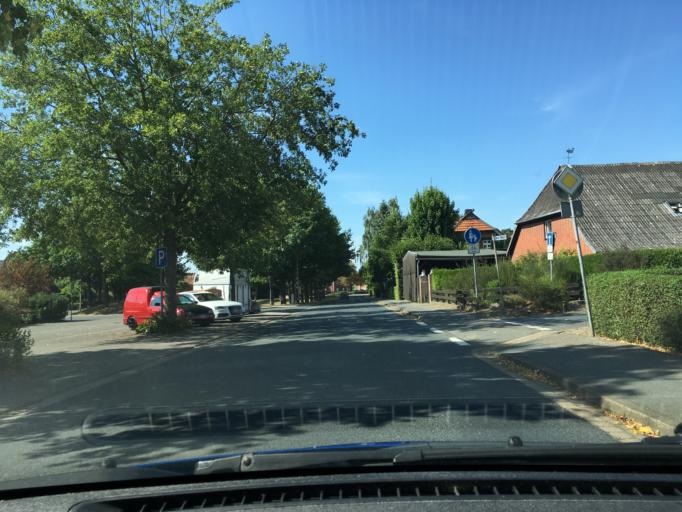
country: DE
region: Lower Saxony
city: Bardowick
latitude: 53.2954
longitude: 10.3873
